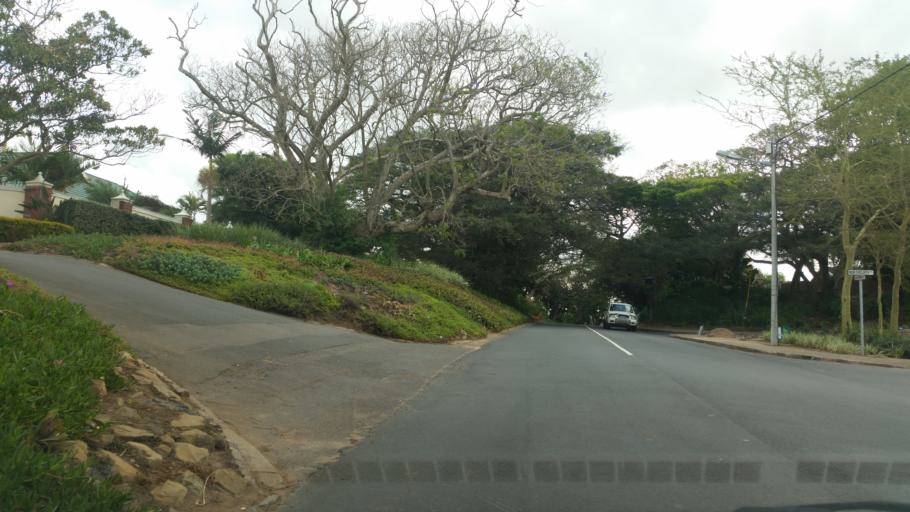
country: ZA
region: KwaZulu-Natal
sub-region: eThekwini Metropolitan Municipality
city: Berea
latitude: -29.8296
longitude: 30.9352
